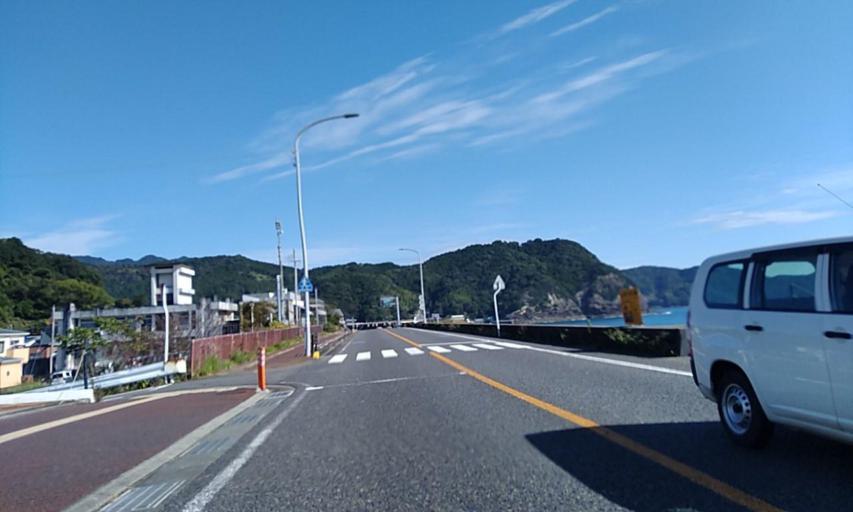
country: JP
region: Wakayama
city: Shingu
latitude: 33.8864
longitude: 136.1000
